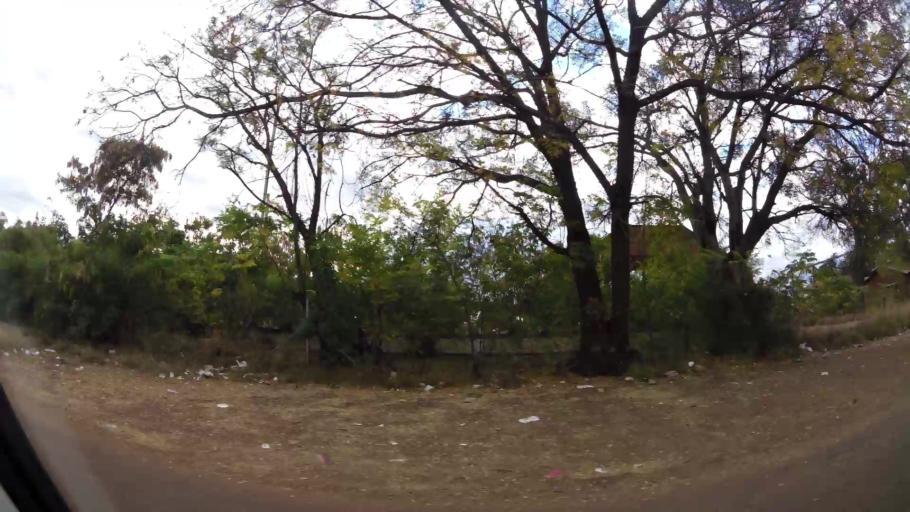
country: ZA
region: Limpopo
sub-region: Waterberg District Municipality
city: Modimolle
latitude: -24.5213
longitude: 28.7141
